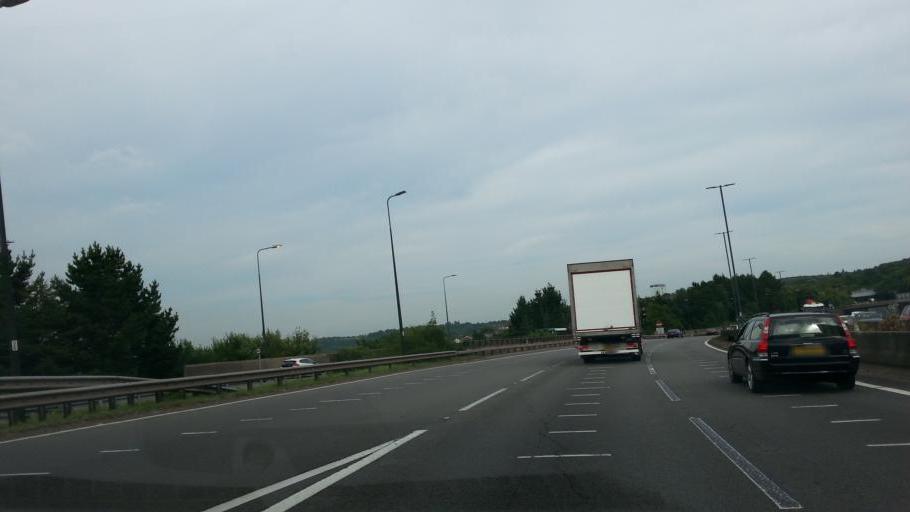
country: GB
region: Wales
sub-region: Newport
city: Newport
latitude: 51.6049
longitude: -2.9847
